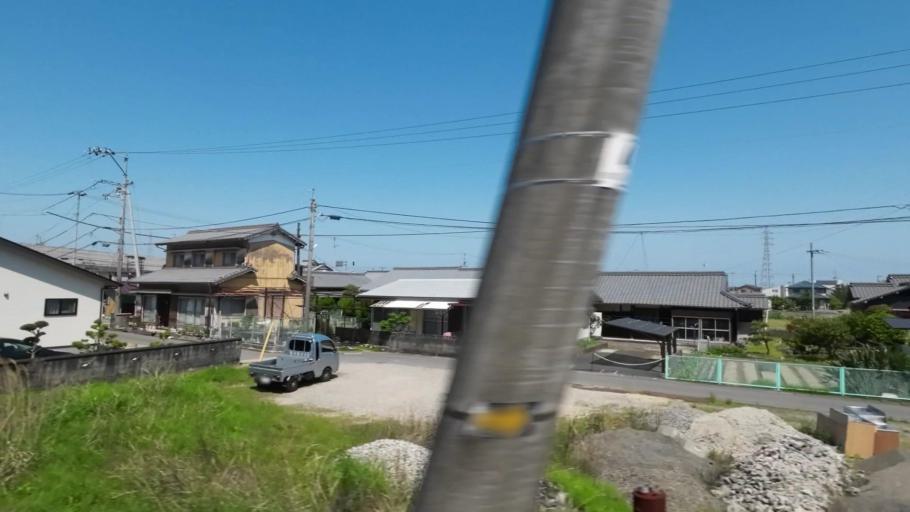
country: JP
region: Ehime
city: Niihama
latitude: 33.9582
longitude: 133.3060
